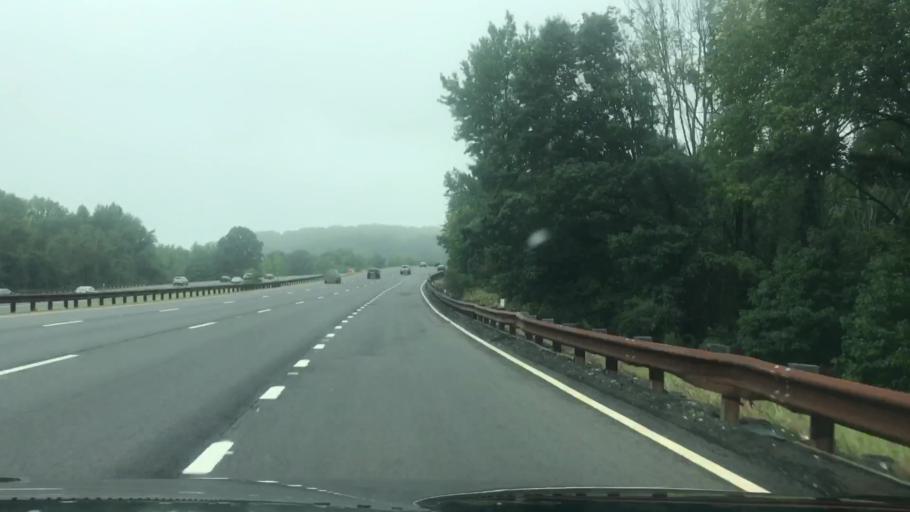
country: US
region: New Jersey
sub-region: Monmouth County
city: Strathmore
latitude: 40.3857
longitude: -74.1725
